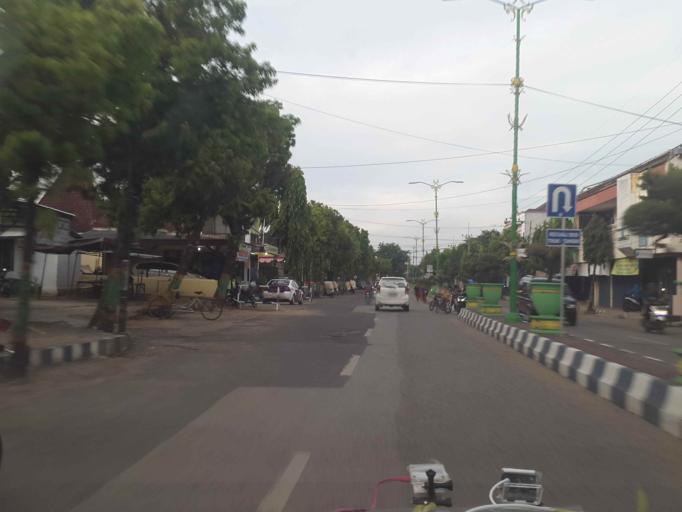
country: ID
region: East Java
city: Sumenep
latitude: -7.0112
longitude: 113.8590
